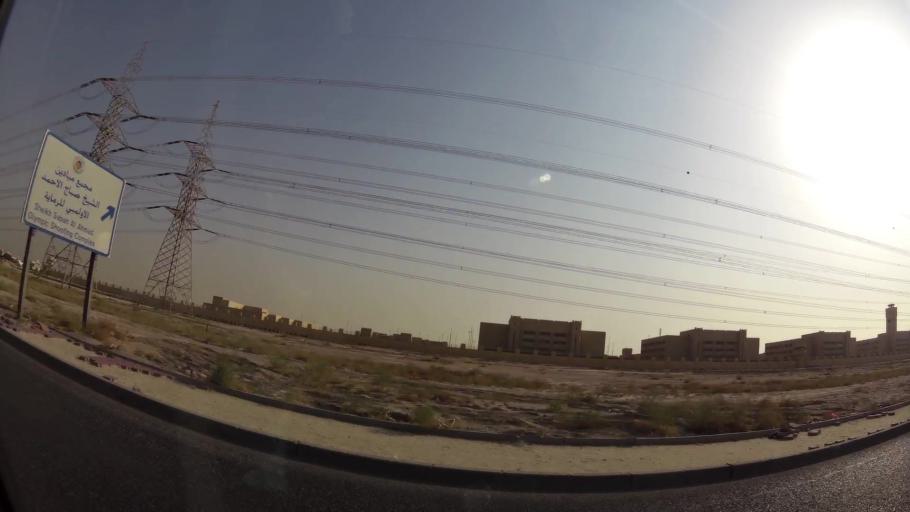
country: KW
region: Al Asimah
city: Ar Rabiyah
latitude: 29.2949
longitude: 47.8609
